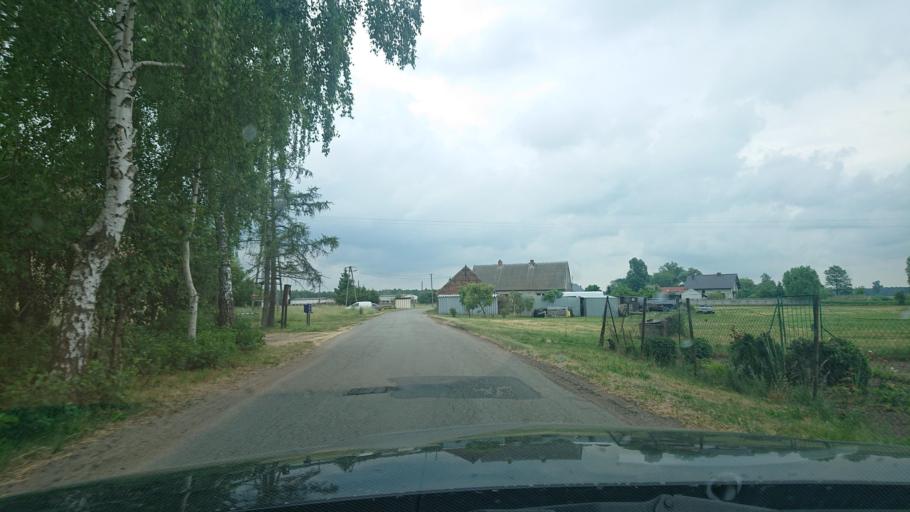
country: PL
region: Greater Poland Voivodeship
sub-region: Powiat gnieznienski
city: Gniezno
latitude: 52.4798
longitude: 17.5462
